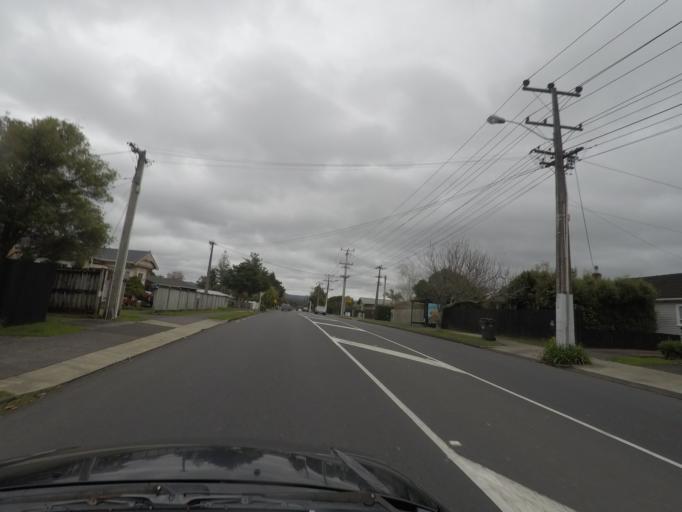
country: NZ
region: Auckland
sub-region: Auckland
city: Waitakere
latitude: -36.9090
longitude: 174.6378
